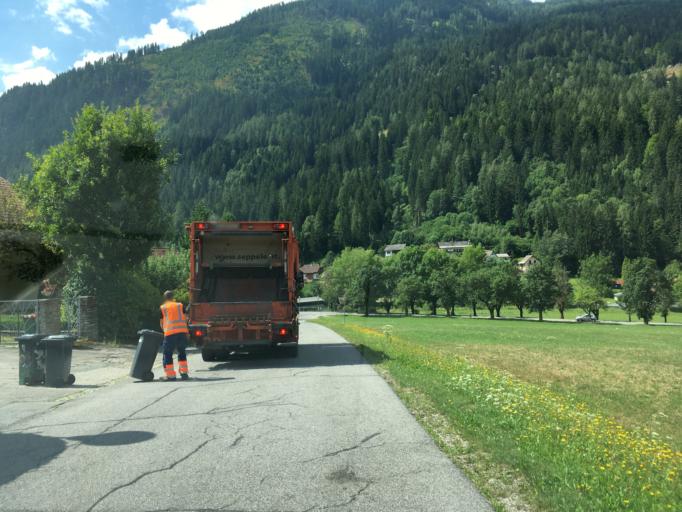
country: AT
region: Carinthia
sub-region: Politischer Bezirk Villach Land
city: Feld am See
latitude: 46.7781
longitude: 13.7464
